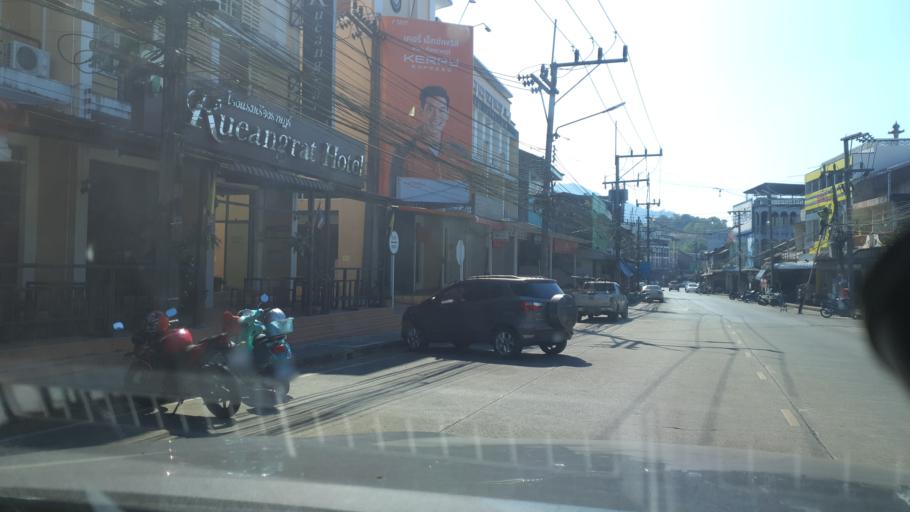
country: TH
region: Ranong
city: Ranong
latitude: 9.9659
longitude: 98.6335
